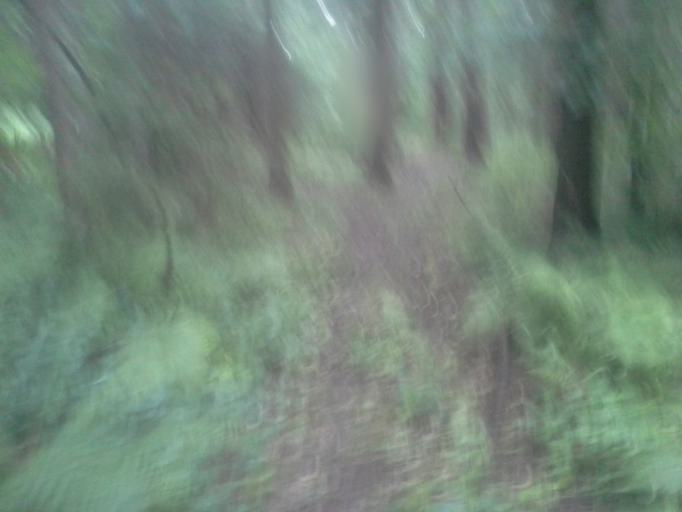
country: RU
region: Moskovskaya
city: Zhavoronki
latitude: 55.6611
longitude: 37.0976
